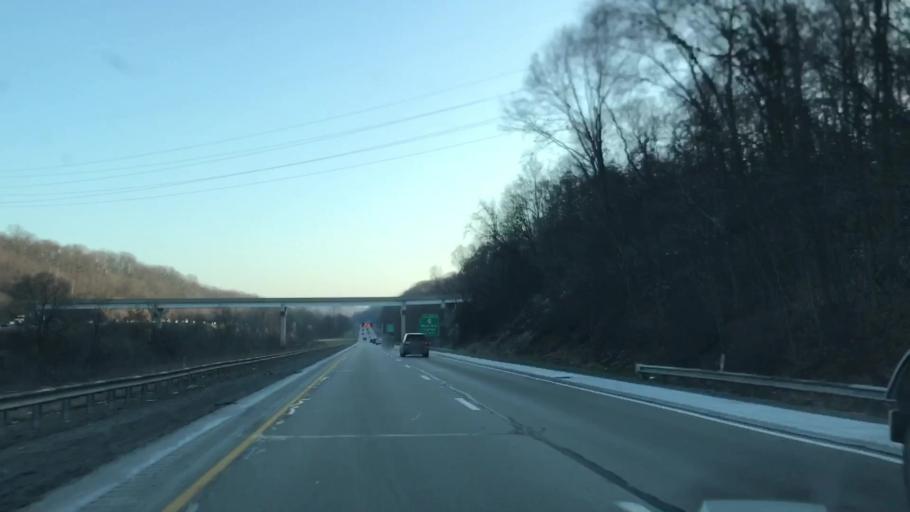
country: US
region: Pennsylvania
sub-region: Allegheny County
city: Emsworth
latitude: 40.4828
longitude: -80.1228
